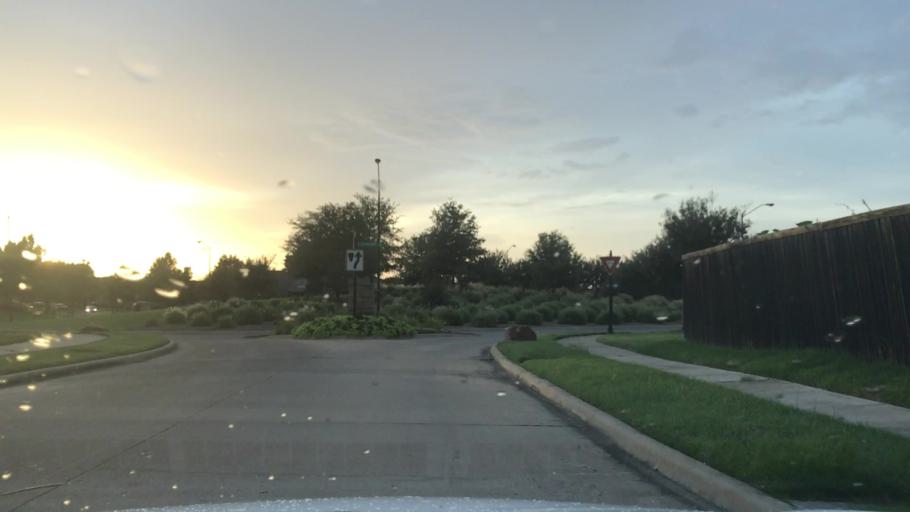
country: US
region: Texas
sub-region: Kaufman County
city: Forney
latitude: 32.7176
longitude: -96.5355
